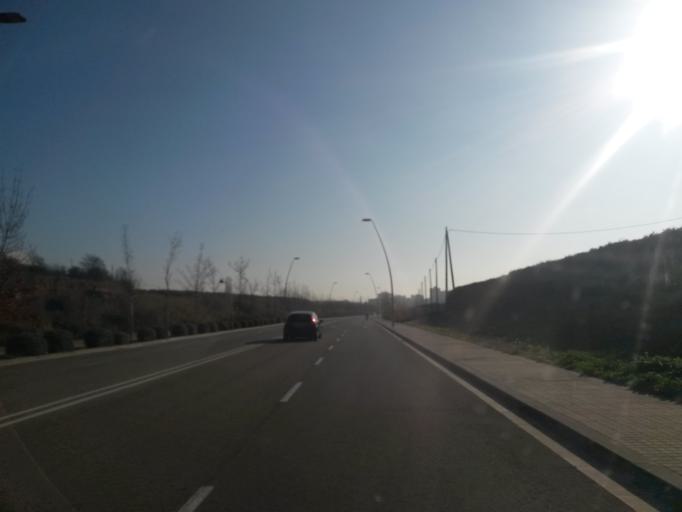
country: ES
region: Catalonia
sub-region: Provincia de Barcelona
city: Barbera del Valles
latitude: 41.5177
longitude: 2.1037
